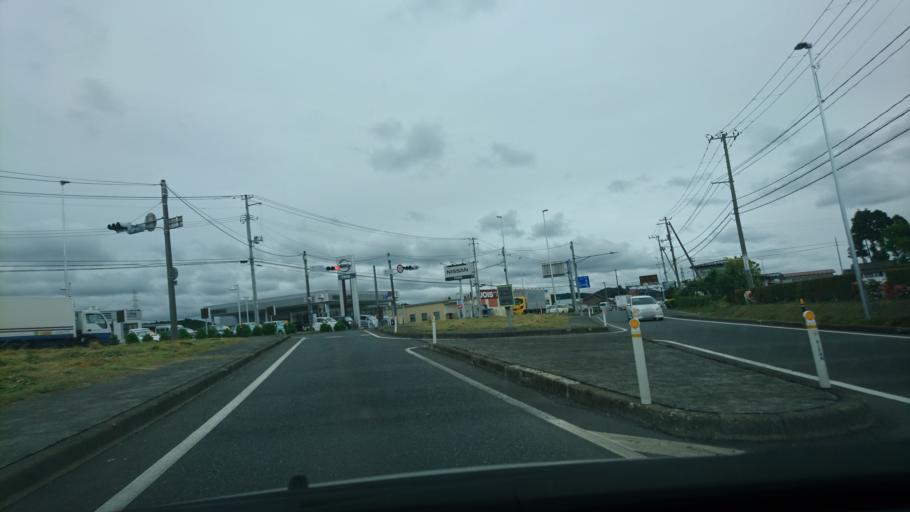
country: JP
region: Iwate
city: Ichinoseki
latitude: 38.9693
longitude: 141.1194
